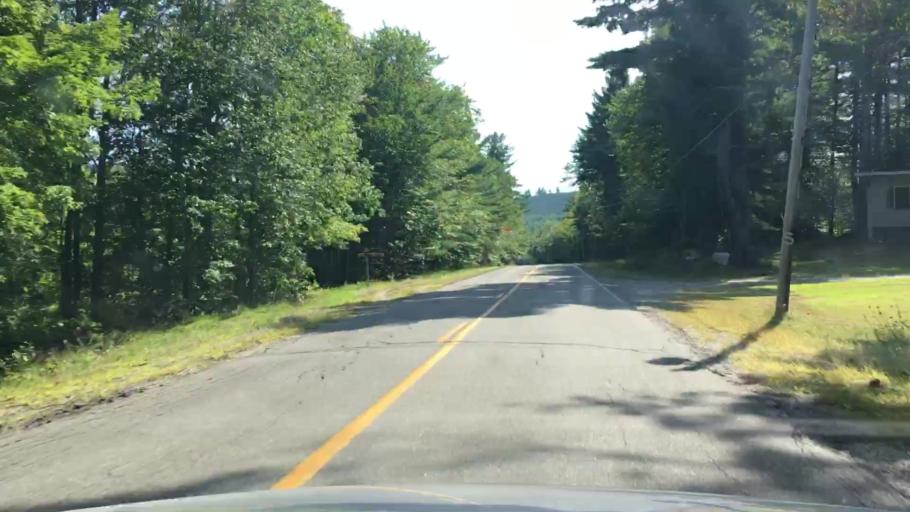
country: US
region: Maine
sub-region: Penobscot County
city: Enfield
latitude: 45.2988
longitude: -68.5520
